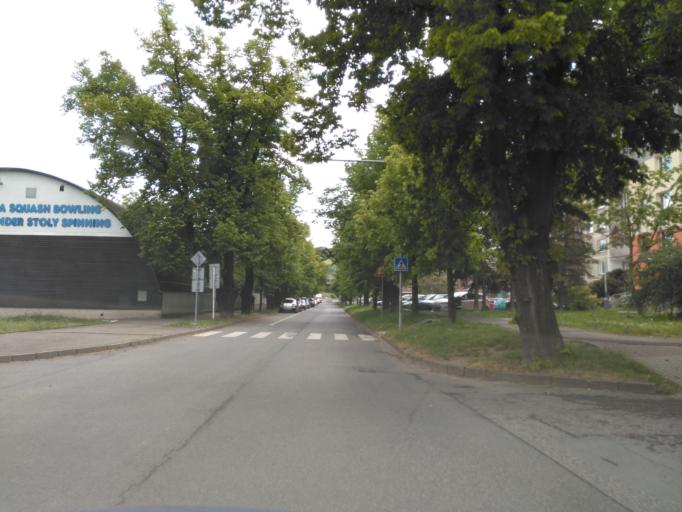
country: CZ
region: Central Bohemia
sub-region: Okres Beroun
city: Beroun
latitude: 49.9607
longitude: 14.0713
